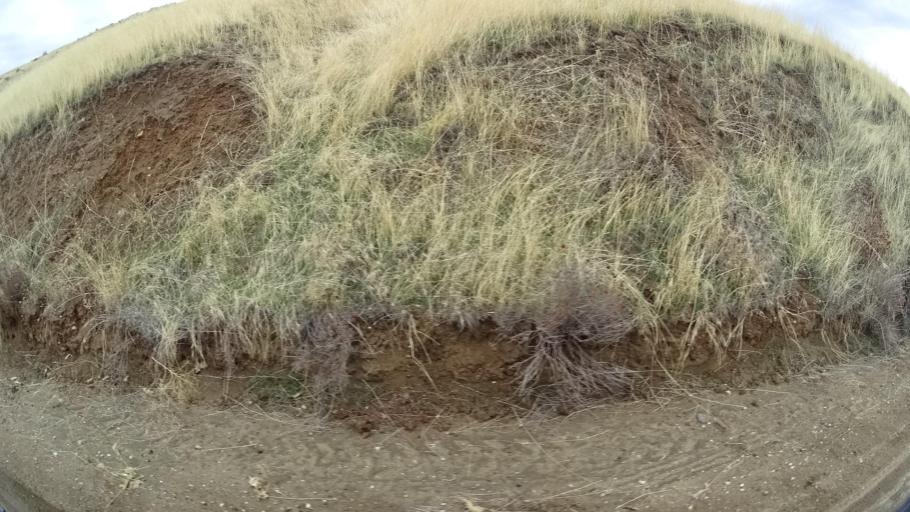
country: US
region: California
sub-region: Kern County
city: Arvin
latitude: 35.1272
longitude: -118.7584
